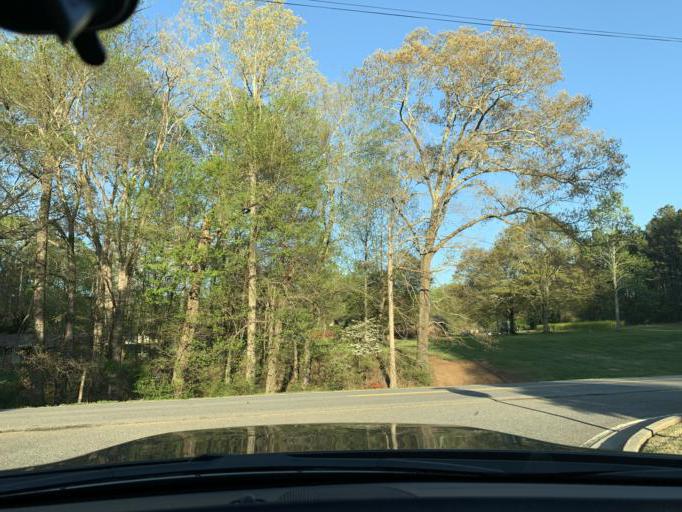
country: US
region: Georgia
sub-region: Forsyth County
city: Cumming
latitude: 34.2460
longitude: -84.1910
